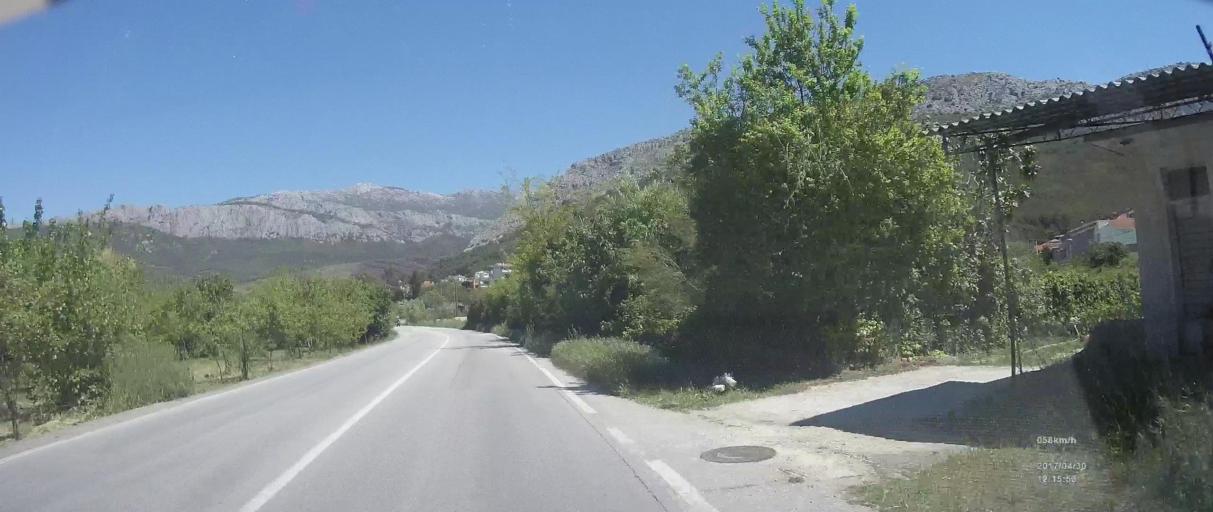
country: HR
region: Splitsko-Dalmatinska
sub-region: Grad Split
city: Stobrec
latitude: 43.5073
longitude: 16.5368
